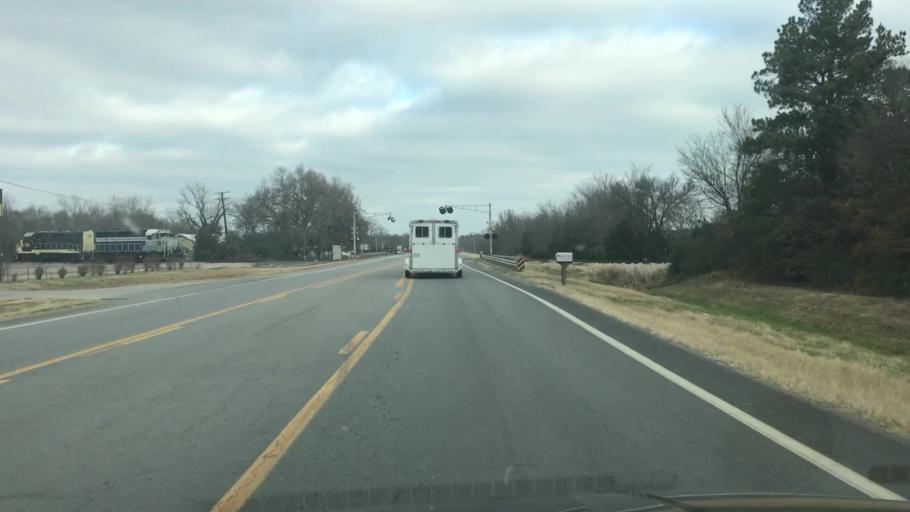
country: US
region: Arkansas
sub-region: Scott County
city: Waldron
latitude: 34.9042
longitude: -94.1074
